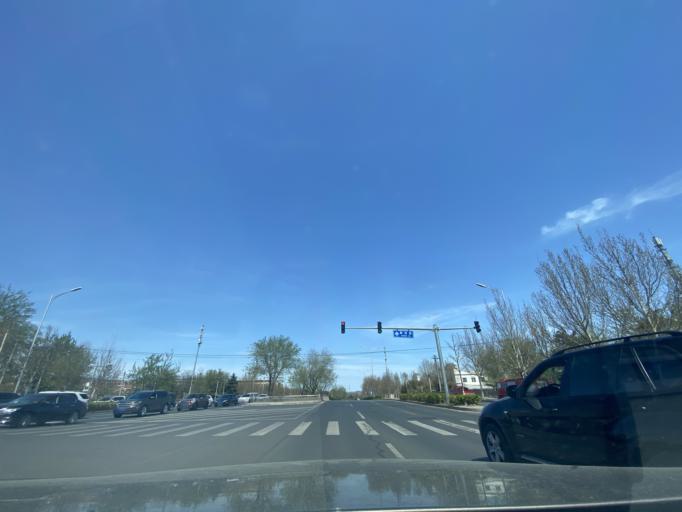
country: CN
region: Beijing
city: Sijiqing
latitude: 39.9390
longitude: 116.2403
